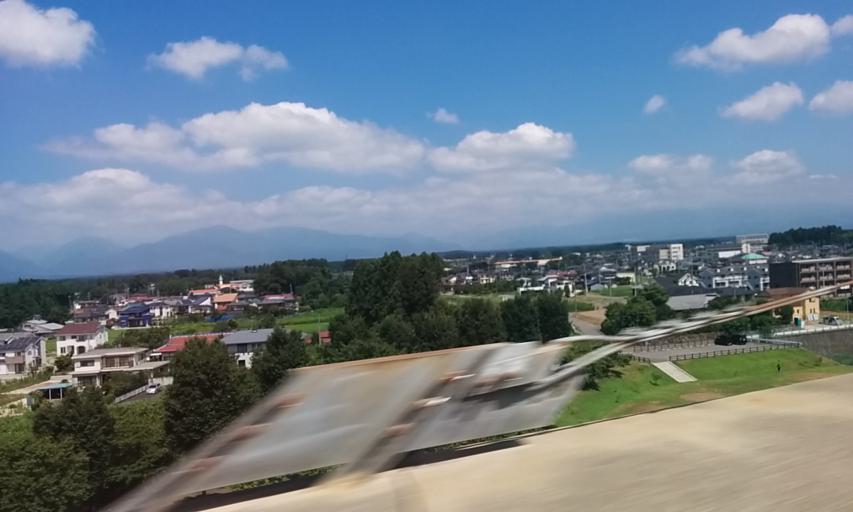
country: JP
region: Tochigi
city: Kuroiso
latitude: 36.9247
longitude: 140.0154
